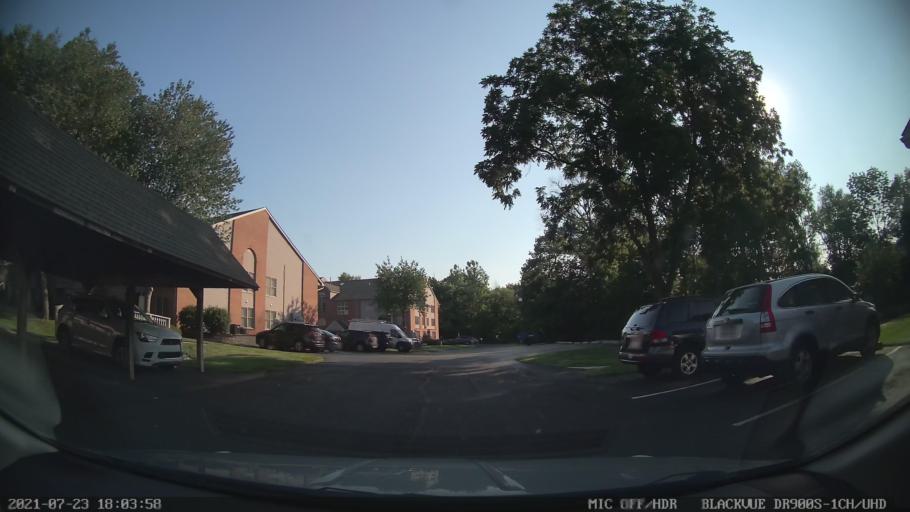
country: US
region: Pennsylvania
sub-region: Lehigh County
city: Emmaus
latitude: 40.5290
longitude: -75.5101
